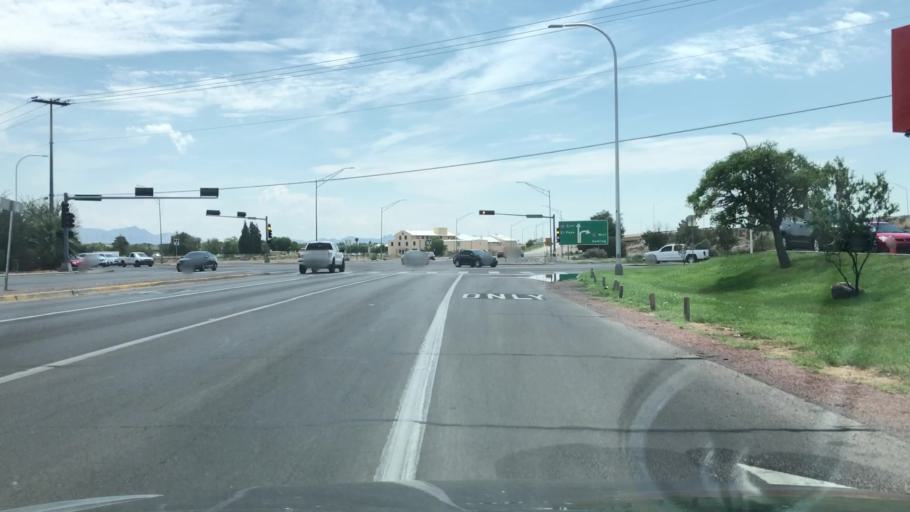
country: US
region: New Mexico
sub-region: Dona Ana County
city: University Park
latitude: 32.2822
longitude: -106.7687
